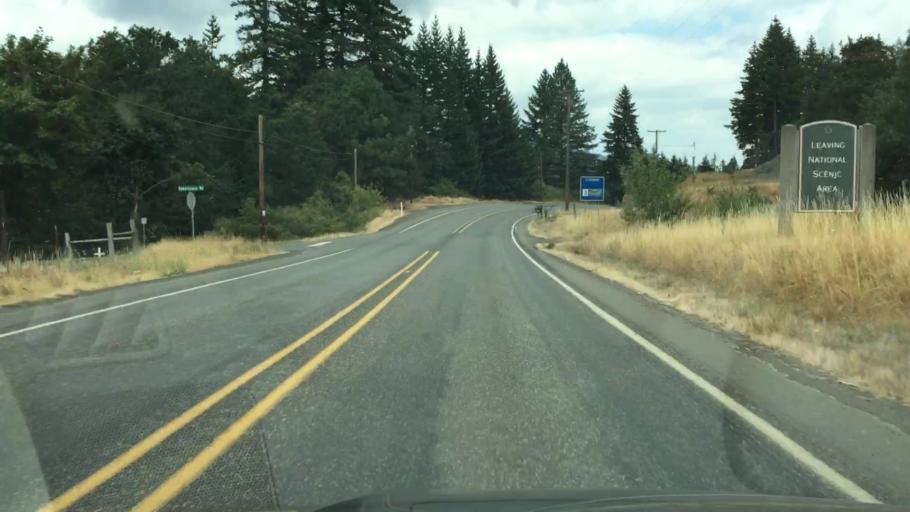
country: US
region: Washington
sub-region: Klickitat County
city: White Salmon
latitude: 45.7648
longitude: -121.5281
